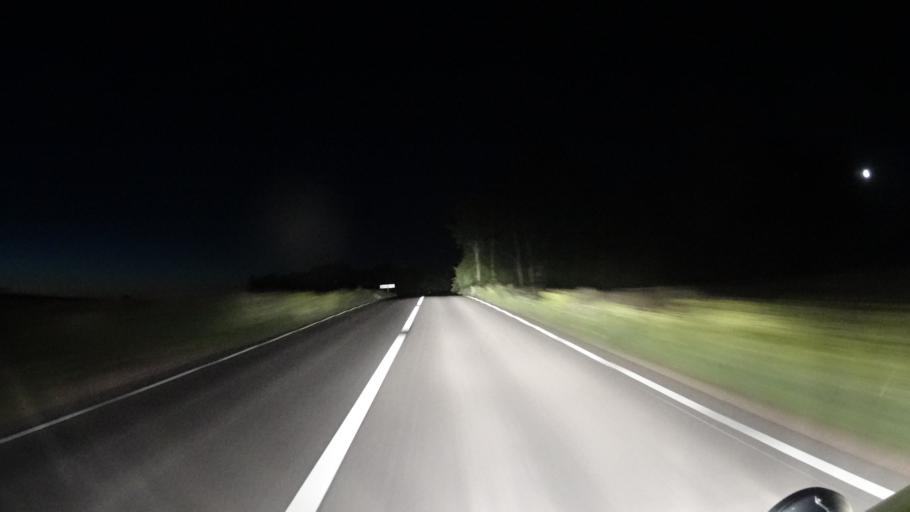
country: SE
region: OEstergoetland
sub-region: Odeshogs Kommun
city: OEdeshoeg
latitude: 58.2433
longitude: 14.7169
